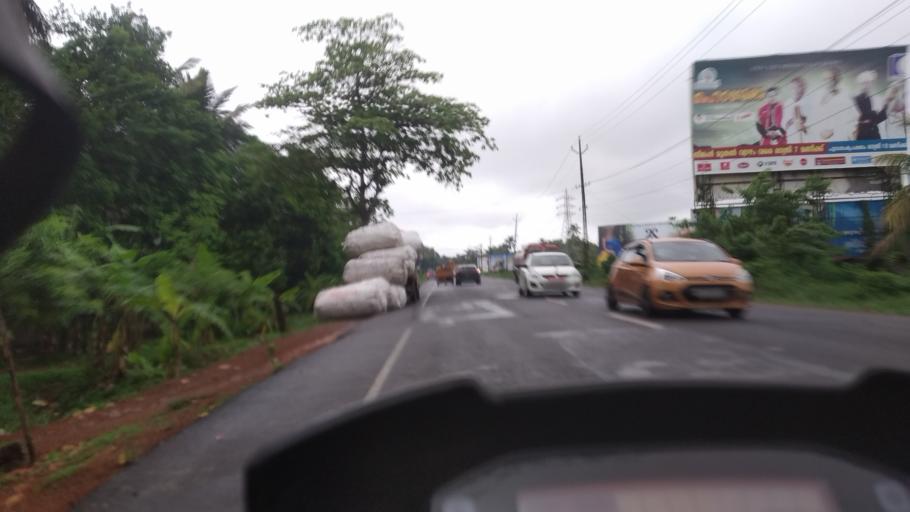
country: IN
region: Kerala
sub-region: Alappuzha
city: Mavelikara
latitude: 9.3175
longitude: 76.4191
